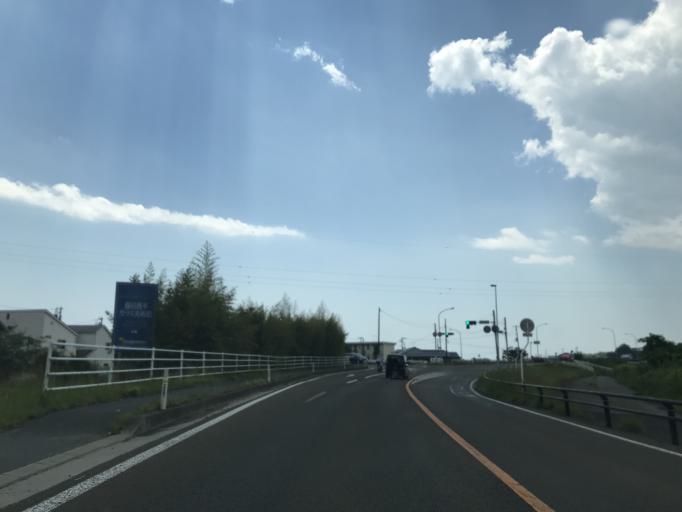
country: JP
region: Miyagi
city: Matsushima
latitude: 38.3917
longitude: 141.0680
